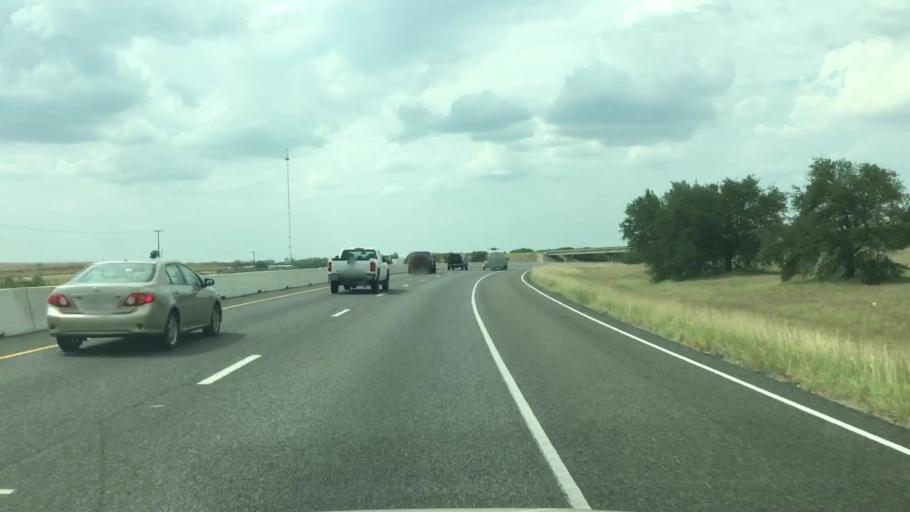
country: US
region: Texas
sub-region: Atascosa County
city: Pleasanton
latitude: 28.9070
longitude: -98.4312
